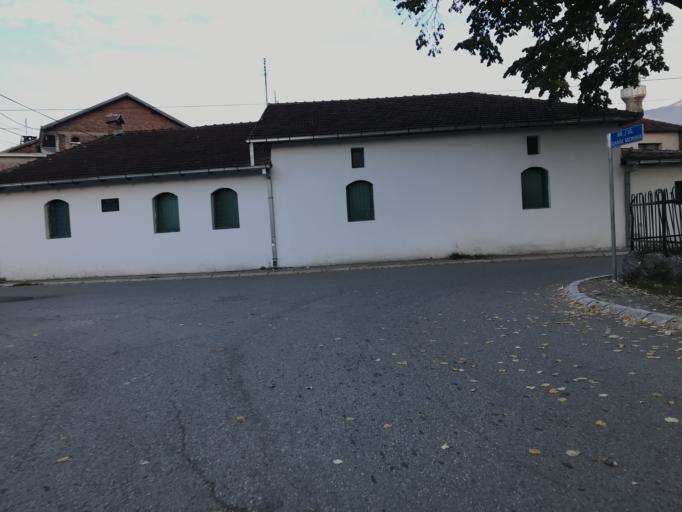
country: XK
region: Pec
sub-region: Komuna e Pejes
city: Peje
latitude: 42.6576
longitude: 20.3014
